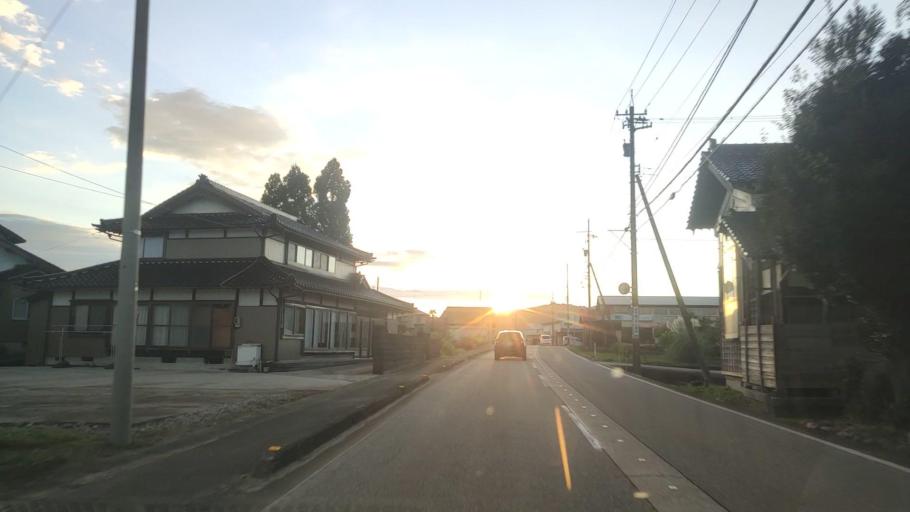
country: JP
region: Toyama
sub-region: Oyabe Shi
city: Oyabe
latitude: 36.6325
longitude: 136.8393
